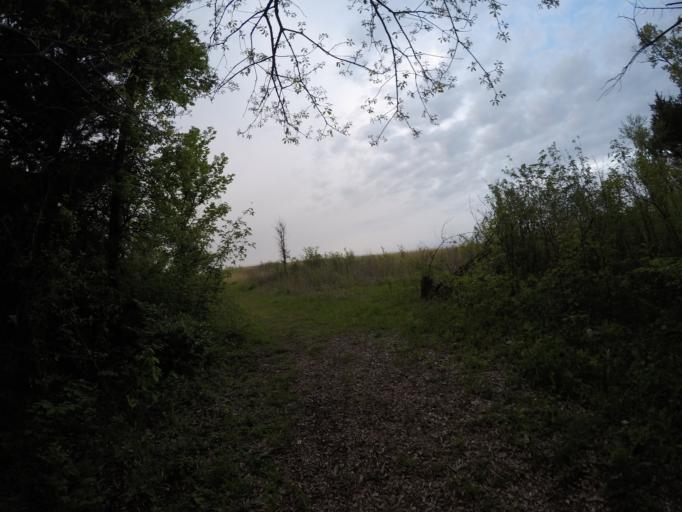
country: US
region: Kansas
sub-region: Riley County
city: Manhattan
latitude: 39.2205
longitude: -96.6248
